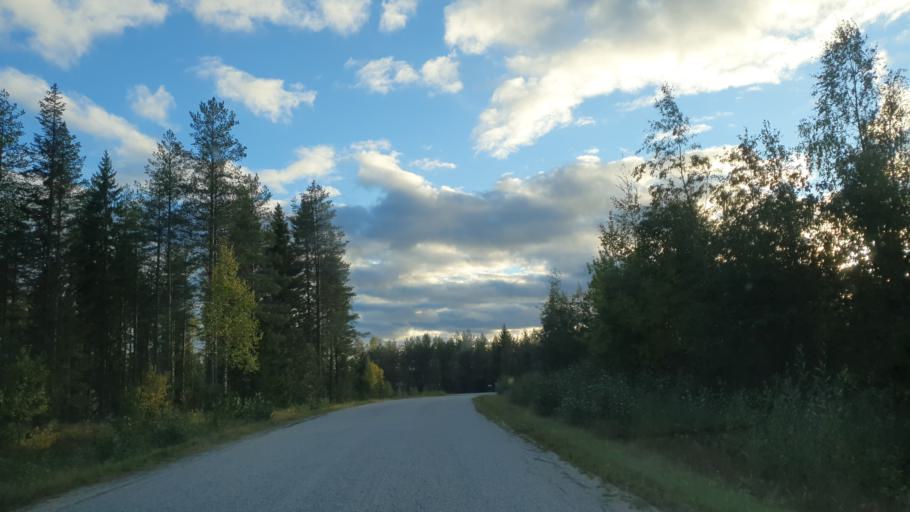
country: FI
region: Kainuu
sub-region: Kehys-Kainuu
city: Kuhmo
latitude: 63.9543
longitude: 29.7225
